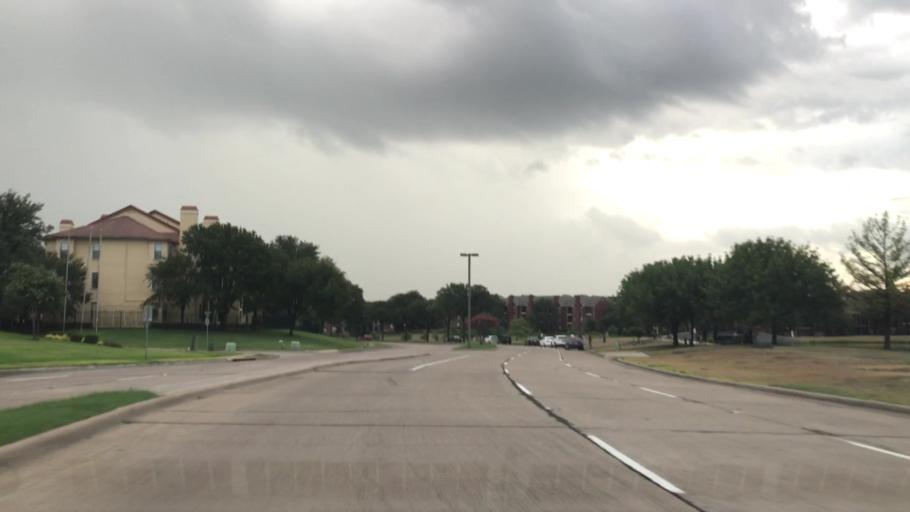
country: US
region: Texas
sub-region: Dallas County
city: Irving
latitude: 32.8813
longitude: -96.9679
